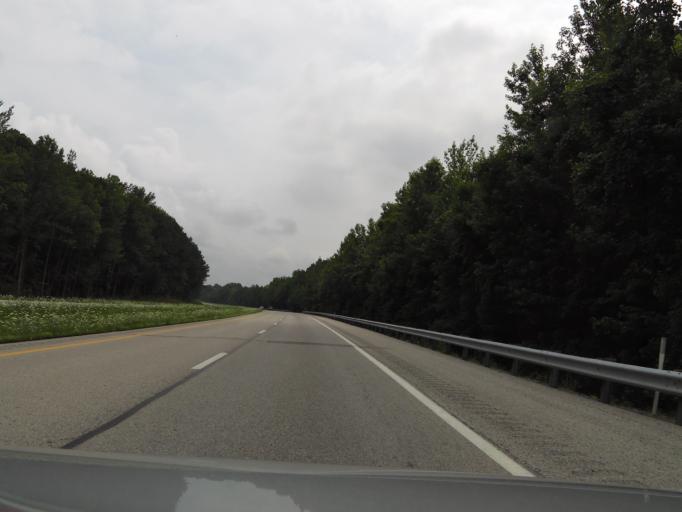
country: US
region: Kentucky
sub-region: Ohio County
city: Beaver Dam
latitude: 37.3518
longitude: -86.8951
